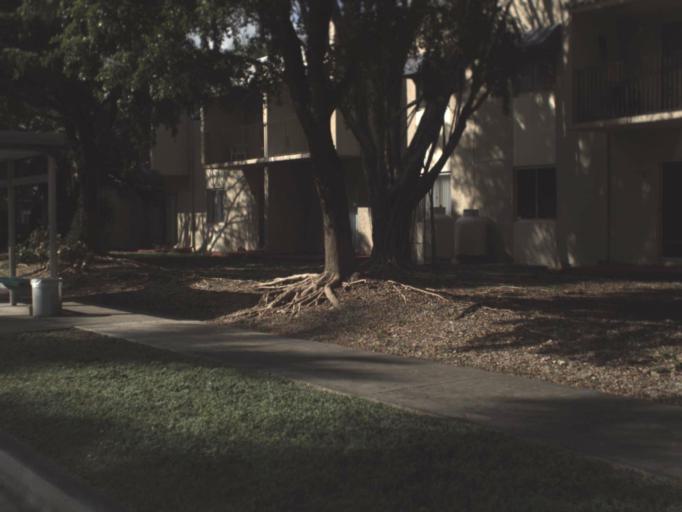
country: US
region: Florida
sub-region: Miami-Dade County
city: Leisure City
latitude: 25.4995
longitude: -80.4437
